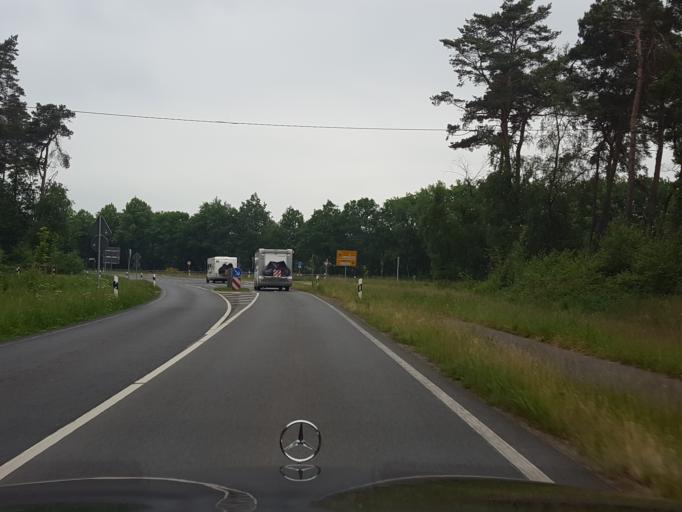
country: DE
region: North Rhine-Westphalia
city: Olfen
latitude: 51.7055
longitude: 7.3508
